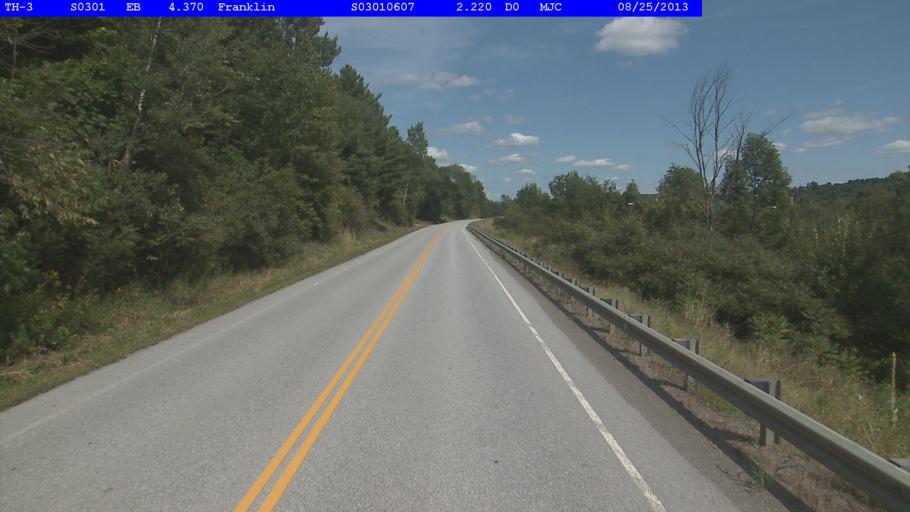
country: CA
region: Quebec
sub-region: Monteregie
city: Bedford
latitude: 44.9758
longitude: -72.9411
